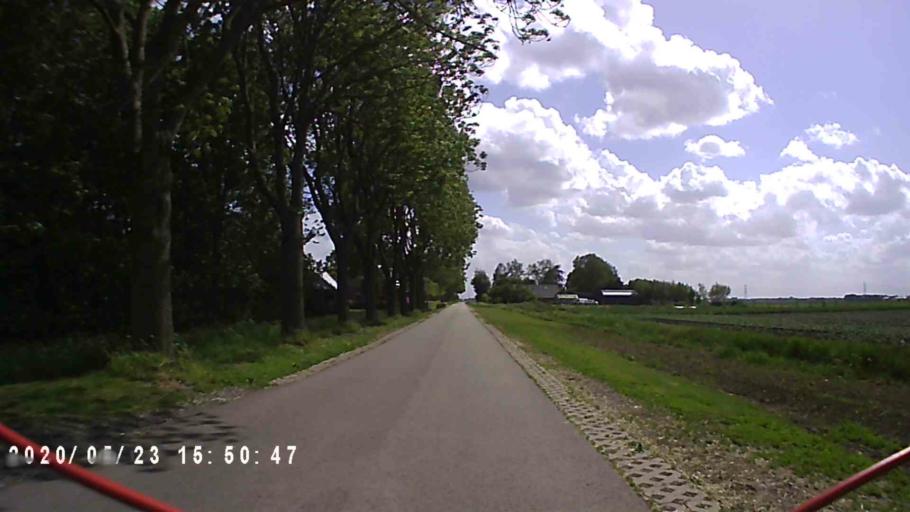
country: NL
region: Groningen
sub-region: Gemeente Delfzijl
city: Delfzijl
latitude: 53.2732
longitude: 6.9049
